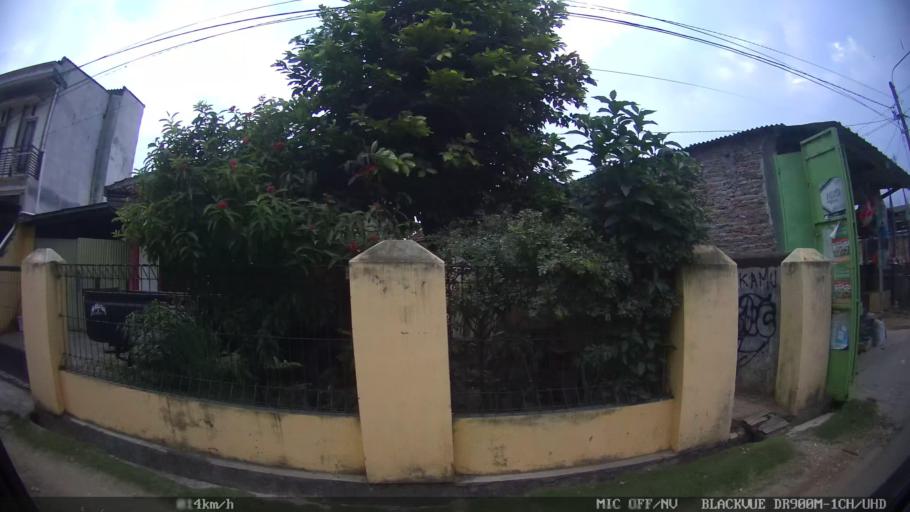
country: ID
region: Lampung
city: Kedaton
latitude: -5.4054
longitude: 105.2882
